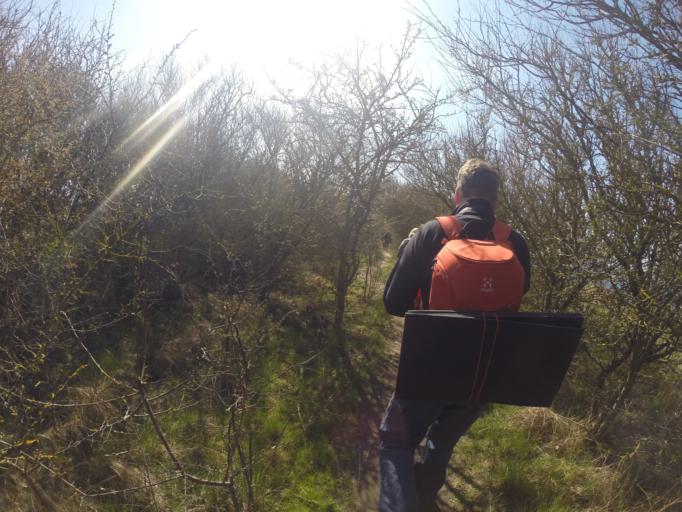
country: DK
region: Zealand
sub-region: Kalundborg Kommune
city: Gorlev
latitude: 55.5278
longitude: 11.0865
